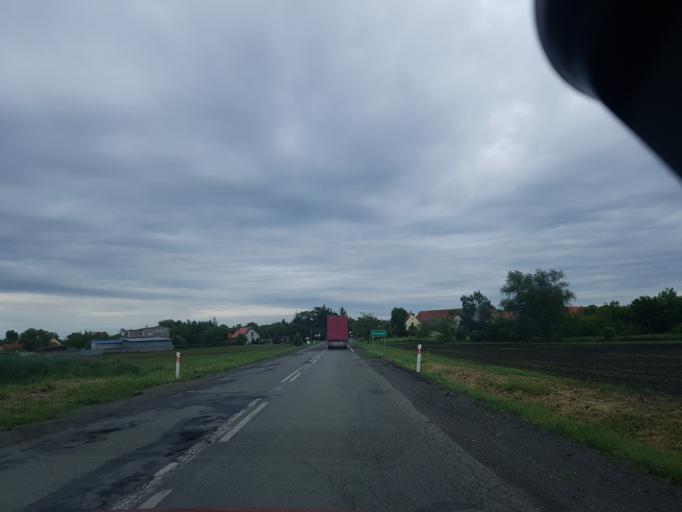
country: PL
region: Lower Silesian Voivodeship
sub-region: Powiat wroclawski
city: Kobierzyce
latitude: 50.9585
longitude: 16.8872
